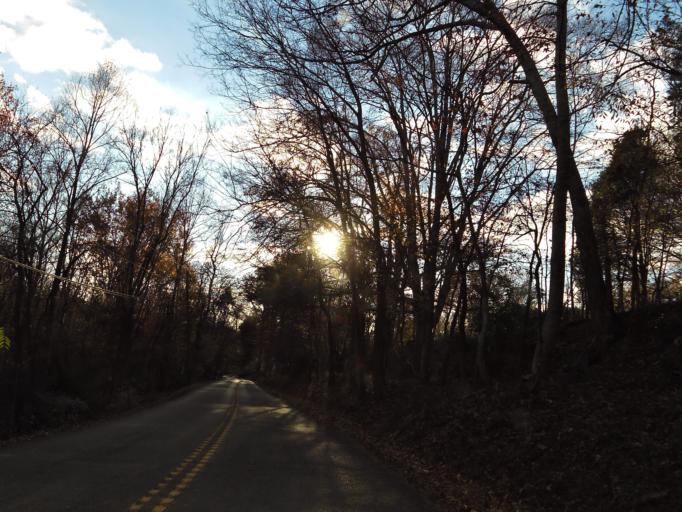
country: US
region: Tennessee
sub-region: Blount County
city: Alcoa
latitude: 35.8711
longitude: -83.9726
